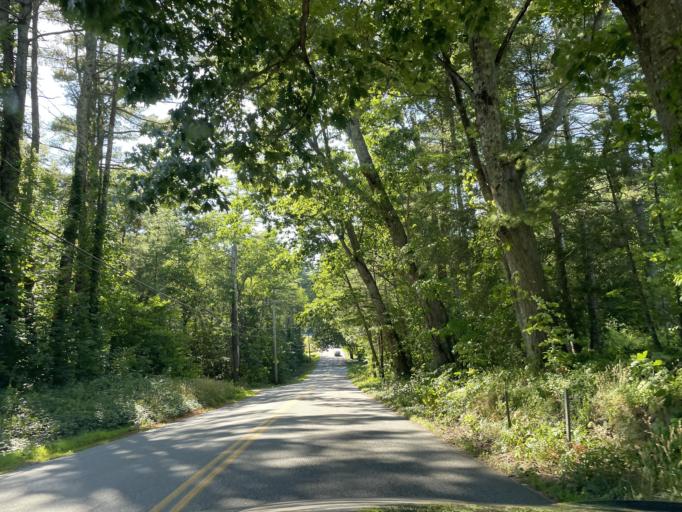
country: US
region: Massachusetts
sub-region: Worcester County
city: Charlton
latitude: 42.1609
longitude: -72.0070
